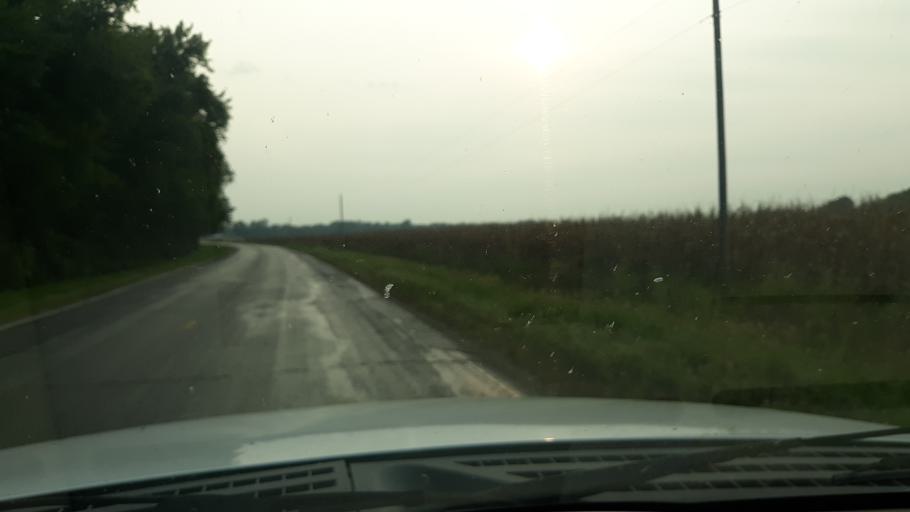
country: US
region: Illinois
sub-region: Edwards County
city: Grayville
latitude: 38.2936
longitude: -87.9691
